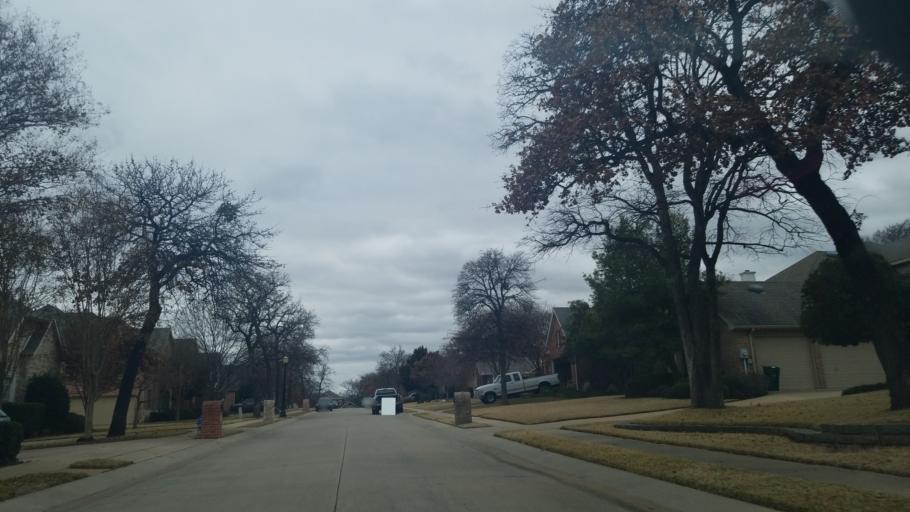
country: US
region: Texas
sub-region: Denton County
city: Corinth
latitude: 33.1347
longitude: -97.0835
